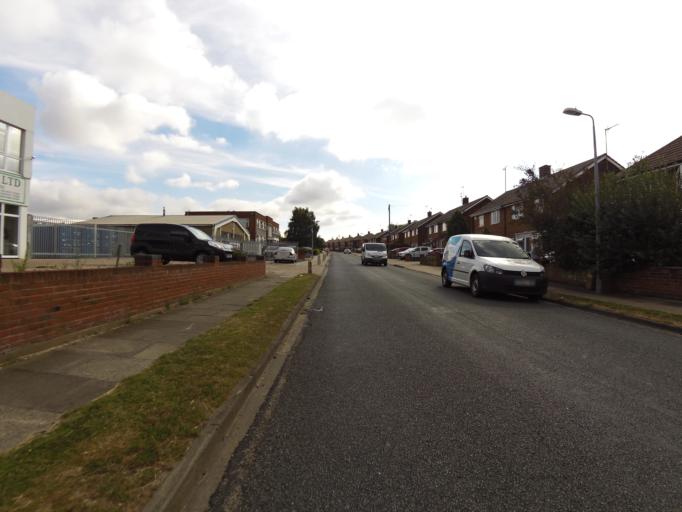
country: GB
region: England
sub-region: Suffolk
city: Ipswich
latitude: 52.0729
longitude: 1.1405
